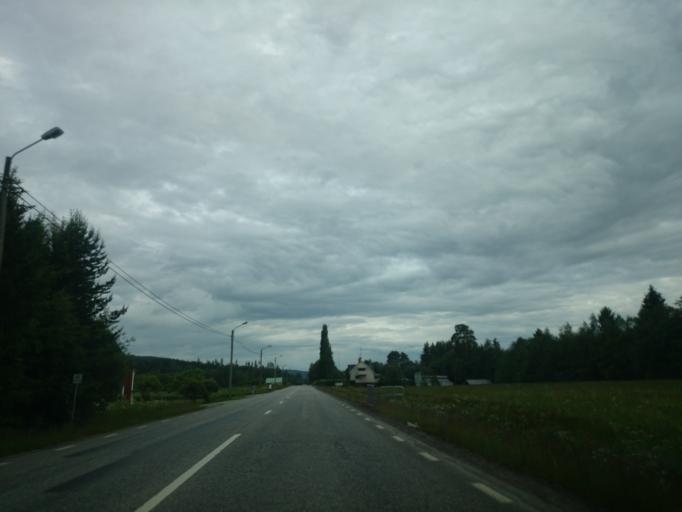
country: SE
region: Vaesternorrland
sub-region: Sundsvalls Kommun
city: Vi
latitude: 62.4552
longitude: 17.1625
